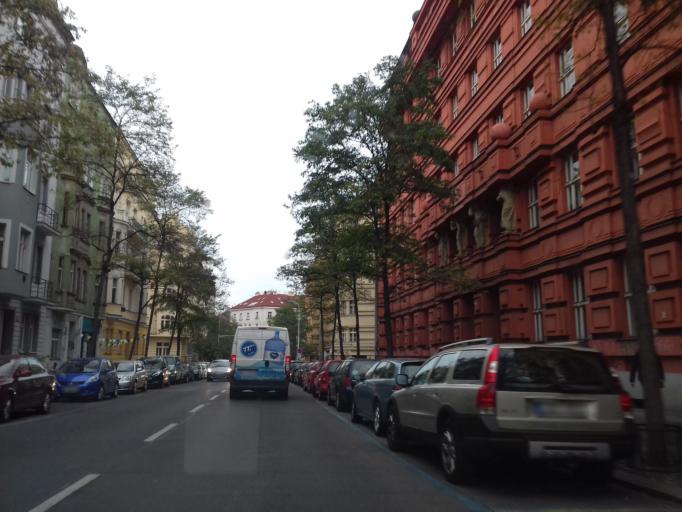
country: CZ
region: Praha
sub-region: Praha 8
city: Karlin
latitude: 50.0802
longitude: 14.4471
